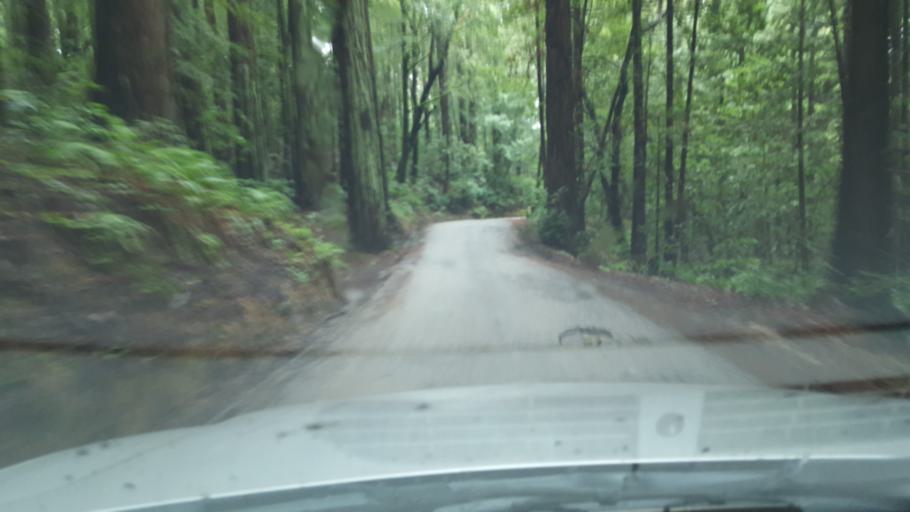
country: US
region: California
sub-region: Santa Cruz County
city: Interlaken
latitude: 37.0119
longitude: -121.7176
